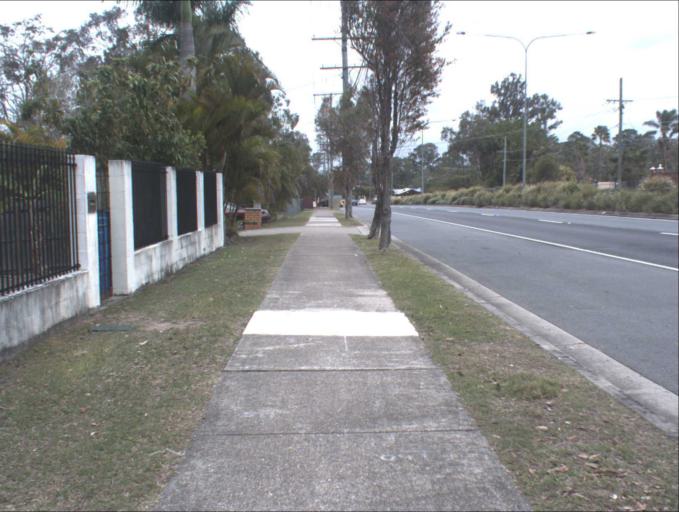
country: AU
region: Queensland
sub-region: Logan
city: Waterford West
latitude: -27.6879
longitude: 153.1240
